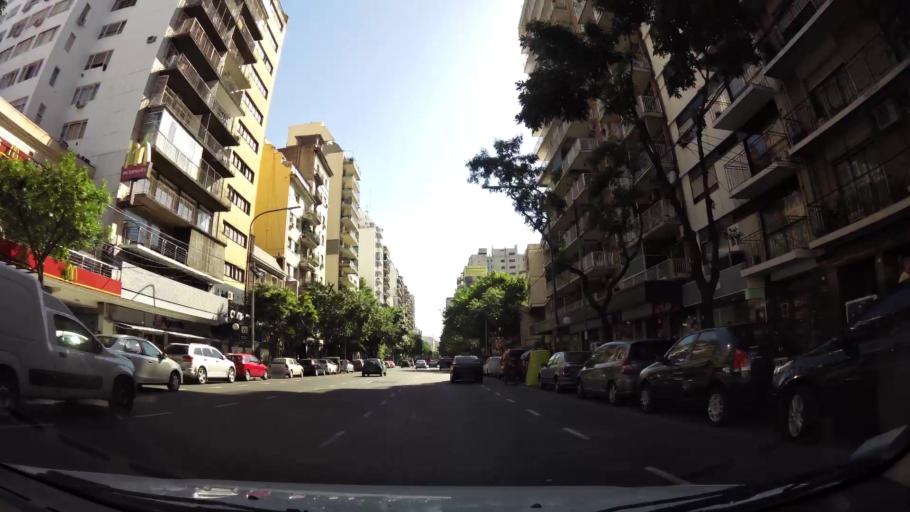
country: AR
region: Buenos Aires F.D.
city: Villa Santa Rita
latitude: -34.6189
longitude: -58.4379
